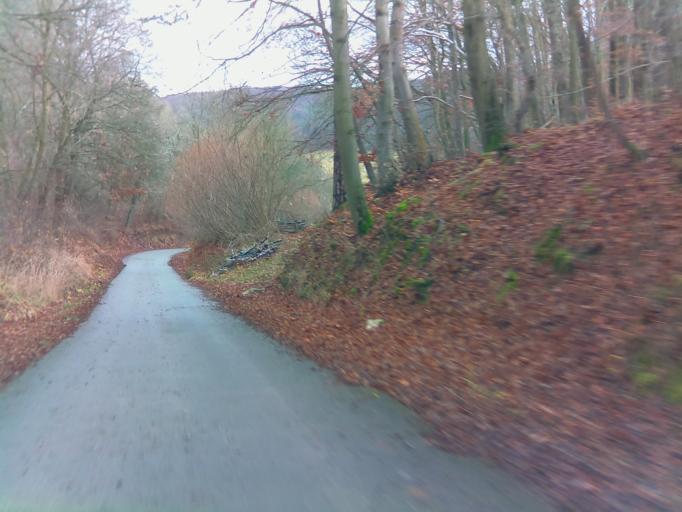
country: DE
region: Thuringia
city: Reinstadt
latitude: 50.7869
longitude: 11.4653
